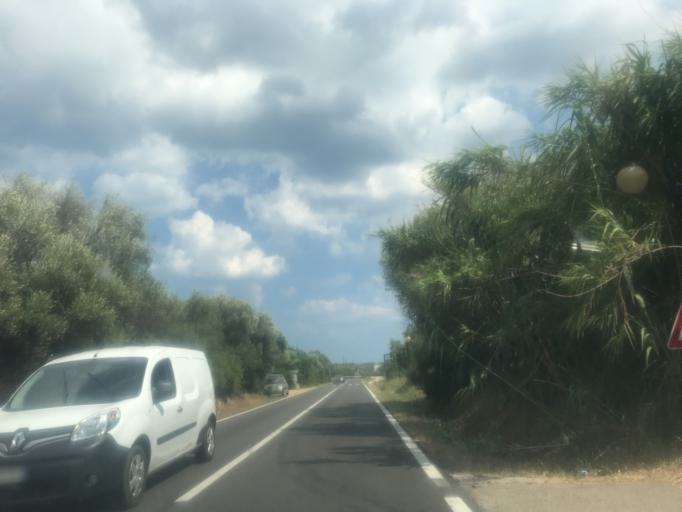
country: IT
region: Sardinia
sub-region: Provincia di Olbia-Tempio
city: San Teodoro
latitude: 40.8356
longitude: 9.6625
